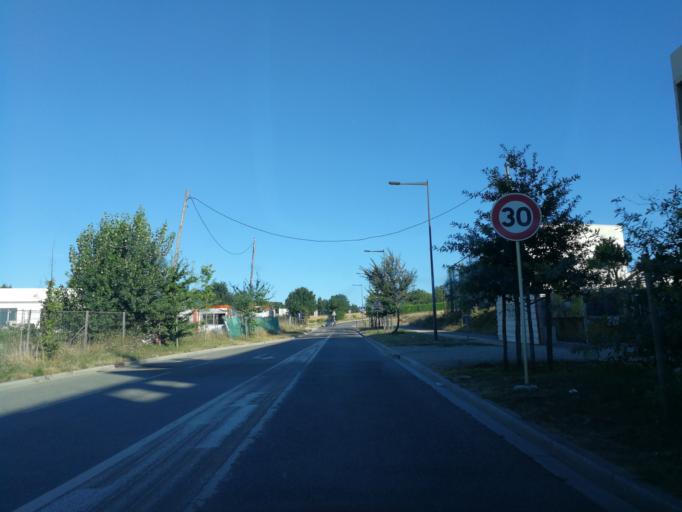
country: FR
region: Midi-Pyrenees
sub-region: Departement de la Haute-Garonne
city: Balma
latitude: 43.6248
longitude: 1.4966
